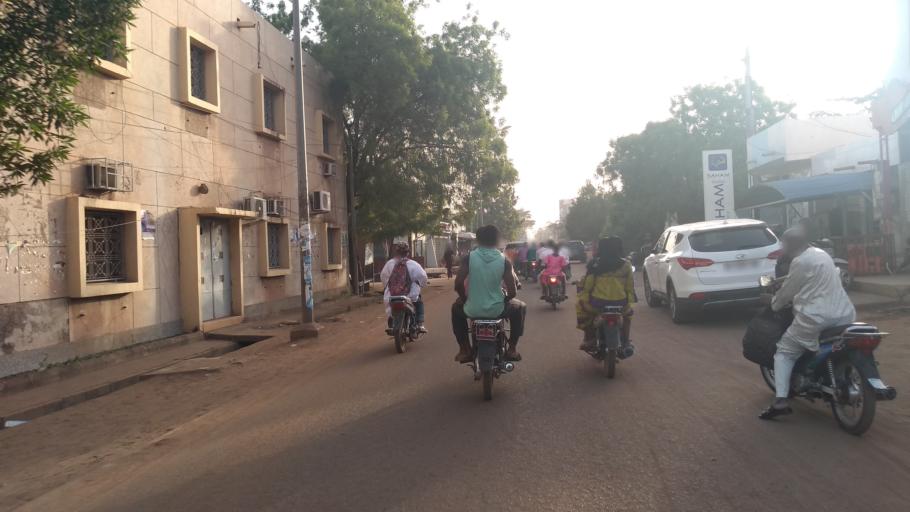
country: ML
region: Bamako
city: Bamako
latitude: 12.6448
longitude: -8.0112
